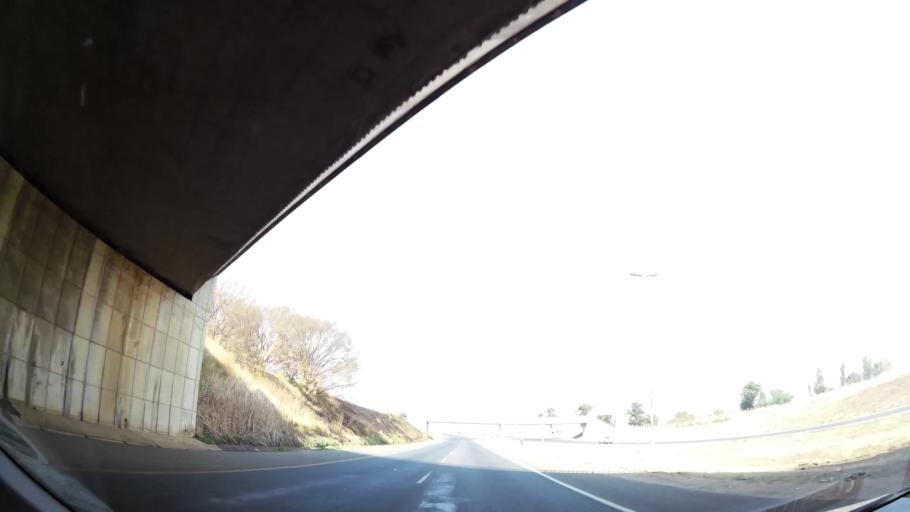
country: ZA
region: Gauteng
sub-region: Ekurhuleni Metropolitan Municipality
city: Brakpan
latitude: -26.1728
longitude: 28.3978
